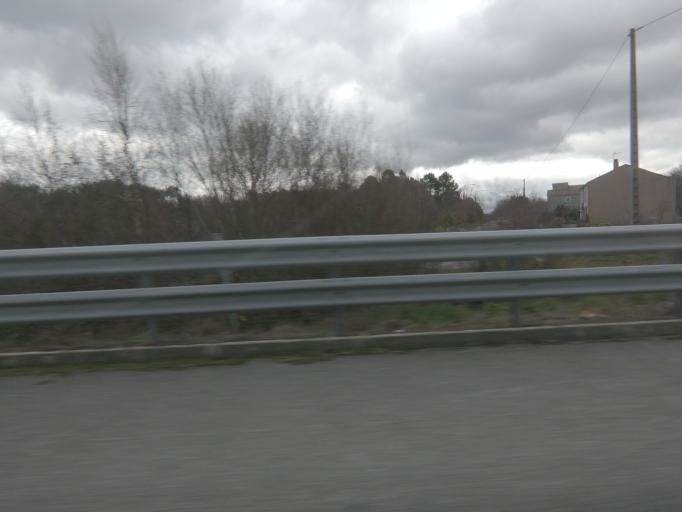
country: ES
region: Galicia
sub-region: Provincia de Ourense
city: Taboadela
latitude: 42.2093
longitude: -7.8319
